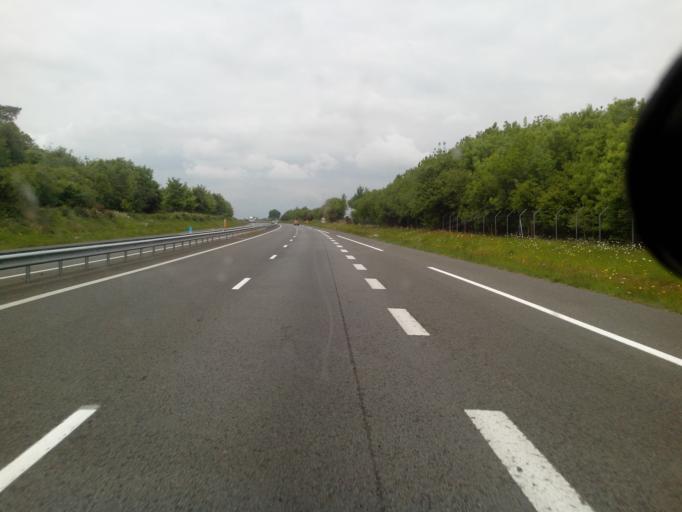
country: FR
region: Brittany
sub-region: Departement d'Ille-et-Vilaine
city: Saint-Sauveur-des-Landes
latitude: 48.3438
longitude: -1.2974
